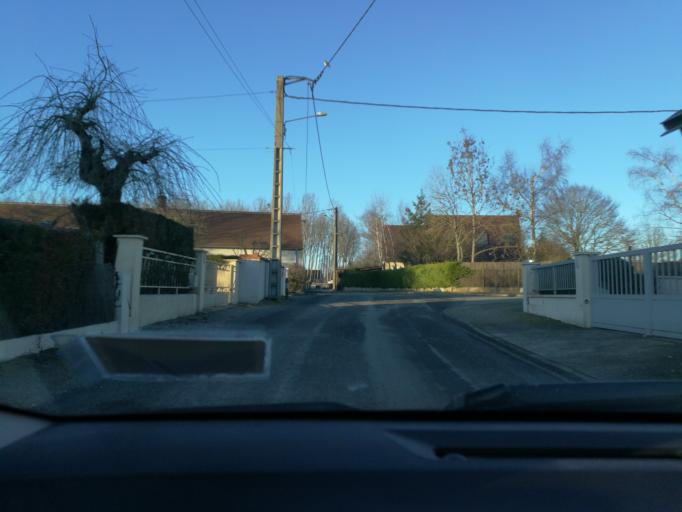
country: FR
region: Centre
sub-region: Departement du Loiret
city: Semoy
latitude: 47.9335
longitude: 1.9656
